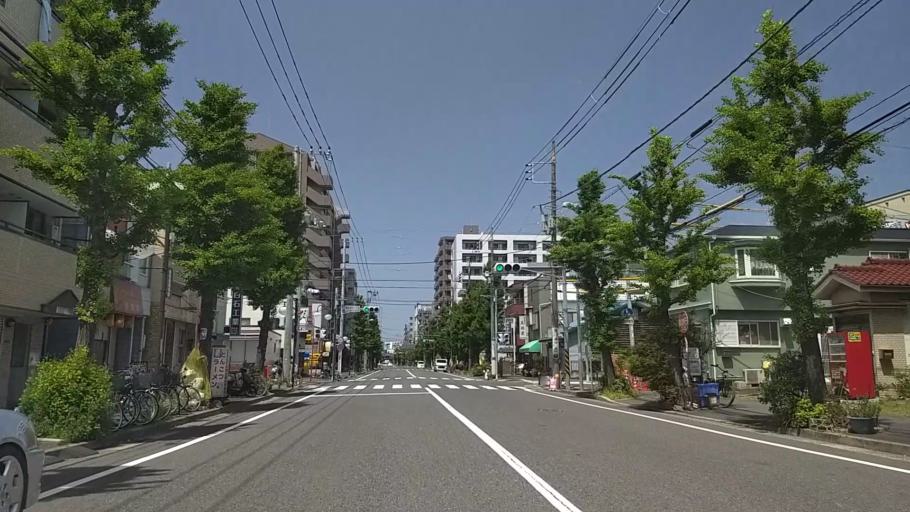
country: JP
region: Kanagawa
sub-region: Kawasaki-shi
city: Kawasaki
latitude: 35.5175
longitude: 139.7140
